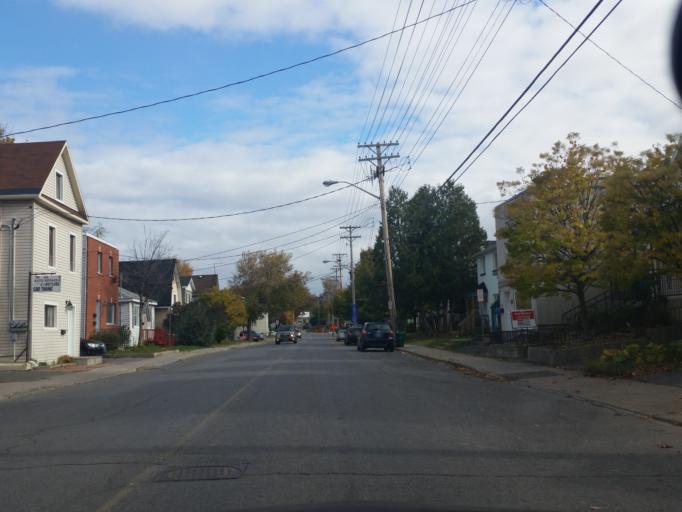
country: CA
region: Ontario
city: Ottawa
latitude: 45.4405
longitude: -75.6672
